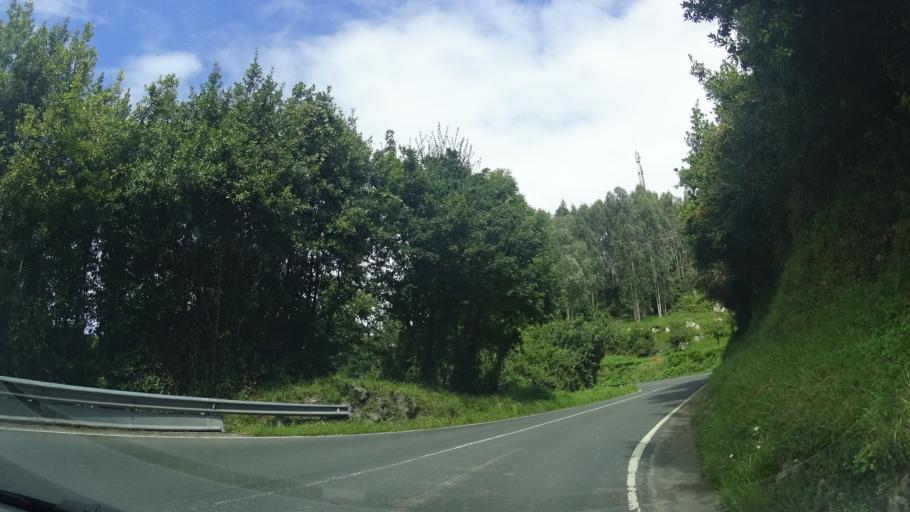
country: ES
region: Asturias
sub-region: Province of Asturias
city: Ribadesella
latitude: 43.4646
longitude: -5.1255
